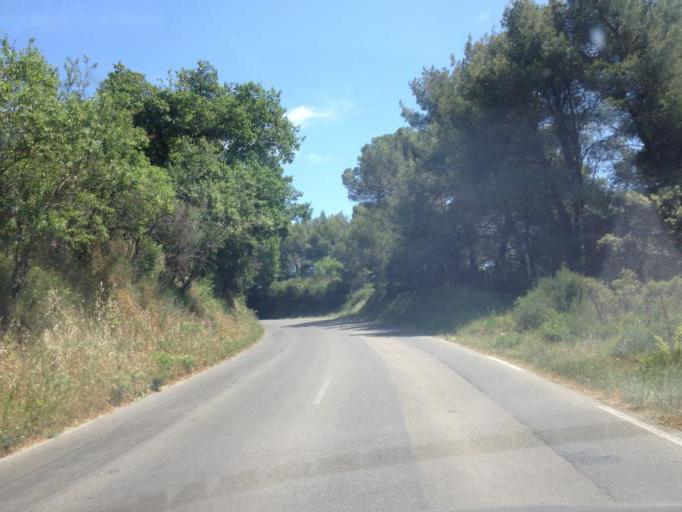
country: FR
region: Provence-Alpes-Cote d'Azur
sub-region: Departement du Vaucluse
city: Cadenet
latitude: 43.7388
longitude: 5.3509
